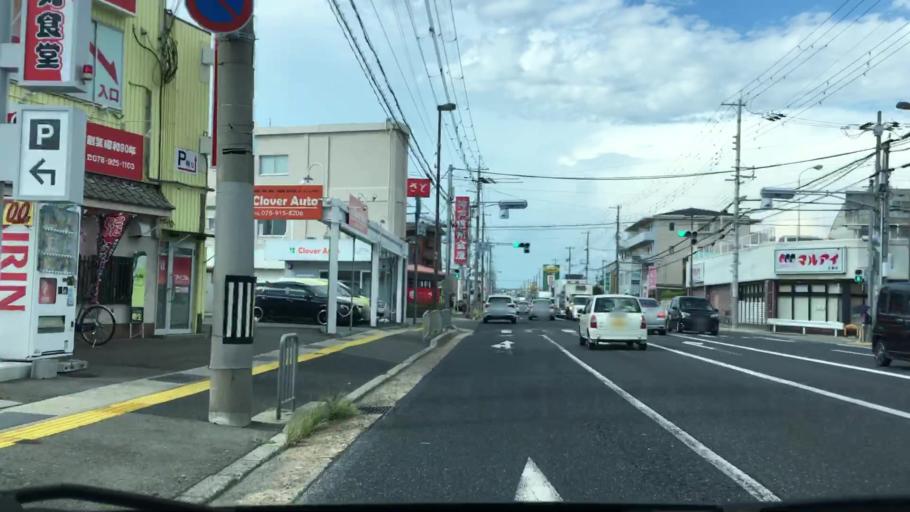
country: JP
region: Hyogo
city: Akashi
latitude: 34.6721
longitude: 134.9815
